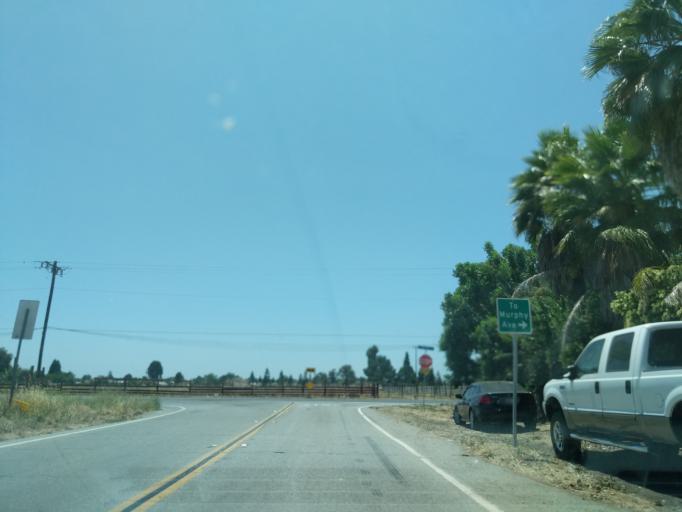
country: US
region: California
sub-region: Santa Clara County
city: San Martin
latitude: 37.1057
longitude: -121.6090
